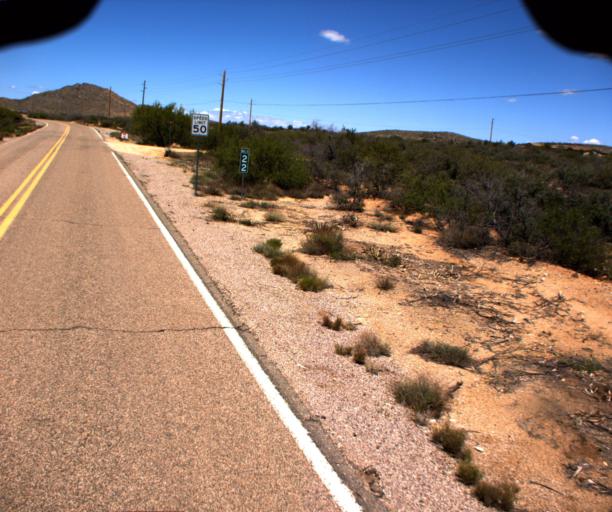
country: US
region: Arizona
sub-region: Yavapai County
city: Congress
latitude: 34.4245
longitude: -112.9161
